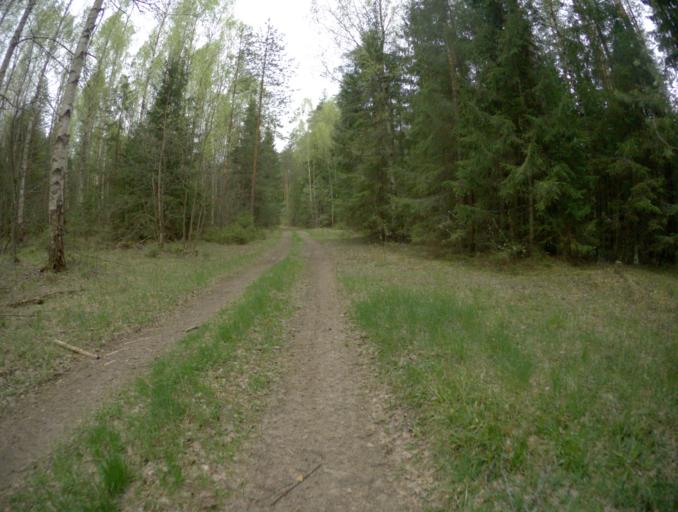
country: RU
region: Vladimir
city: Golovino
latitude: 55.9011
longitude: 40.4384
